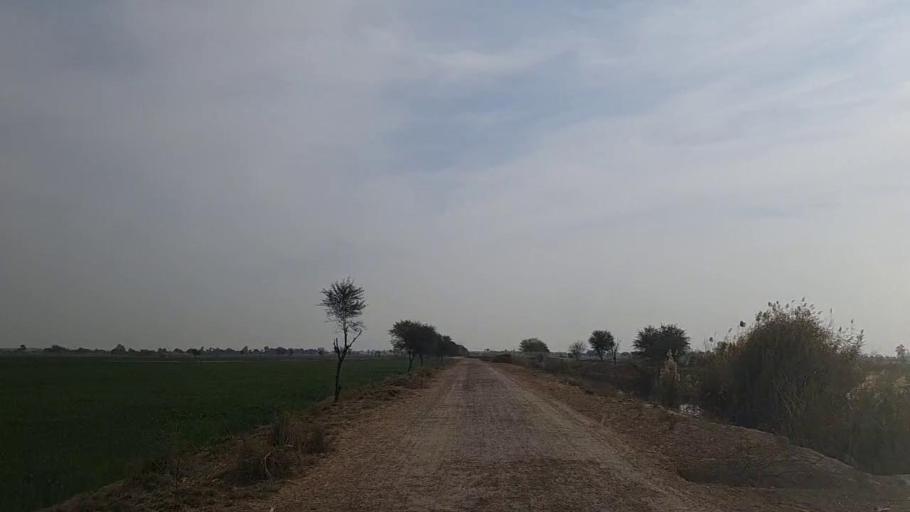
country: PK
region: Sindh
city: Daur
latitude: 26.4451
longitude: 68.4201
